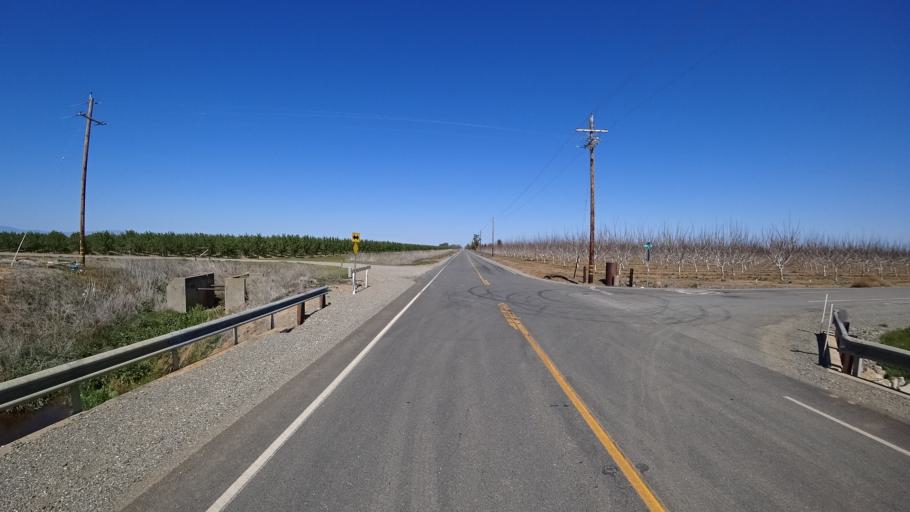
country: US
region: California
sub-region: Glenn County
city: Willows
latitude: 39.4947
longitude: -122.2491
